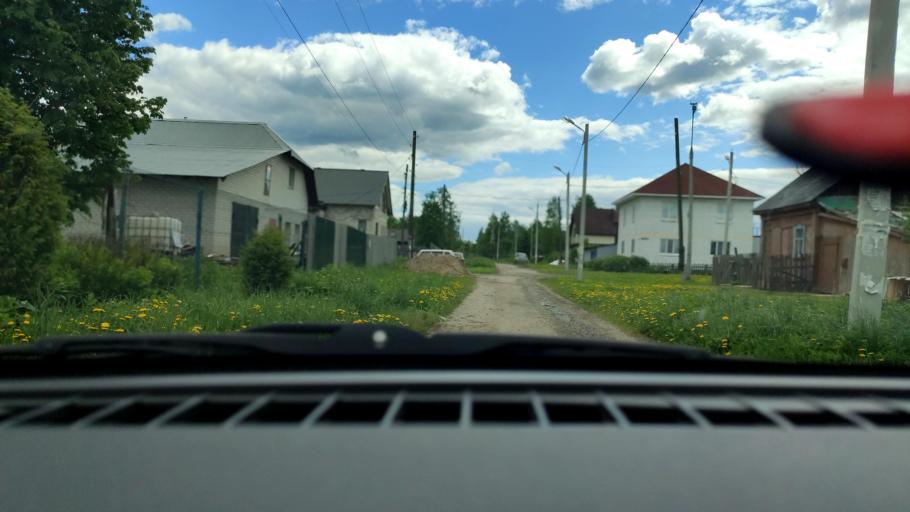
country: RU
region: Perm
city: Perm
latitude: 58.0470
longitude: 56.3610
